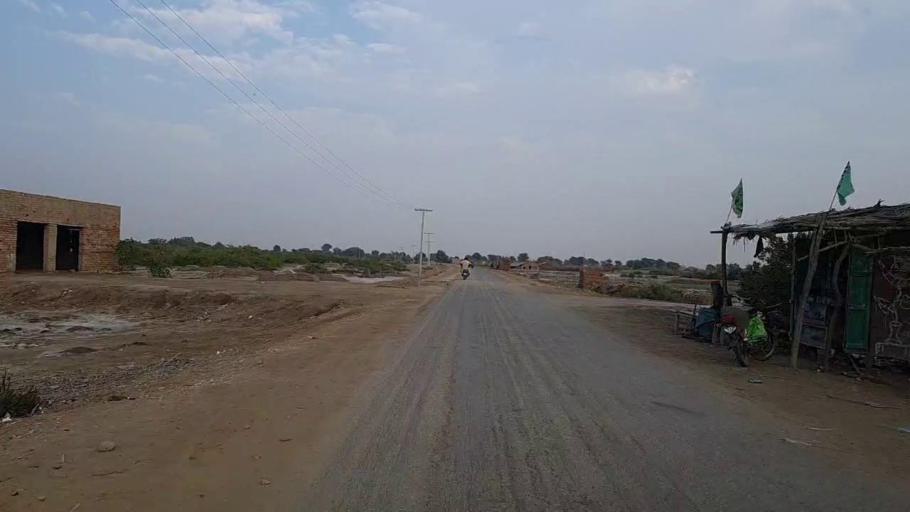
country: PK
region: Sindh
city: Samaro
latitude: 25.3824
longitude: 69.3356
